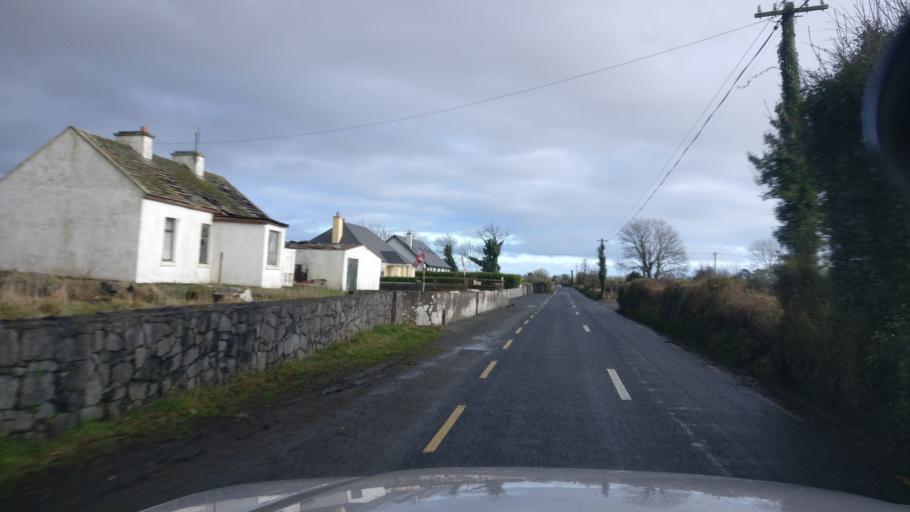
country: IE
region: Connaught
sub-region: County Galway
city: Athenry
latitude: 53.2919
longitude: -8.6387
